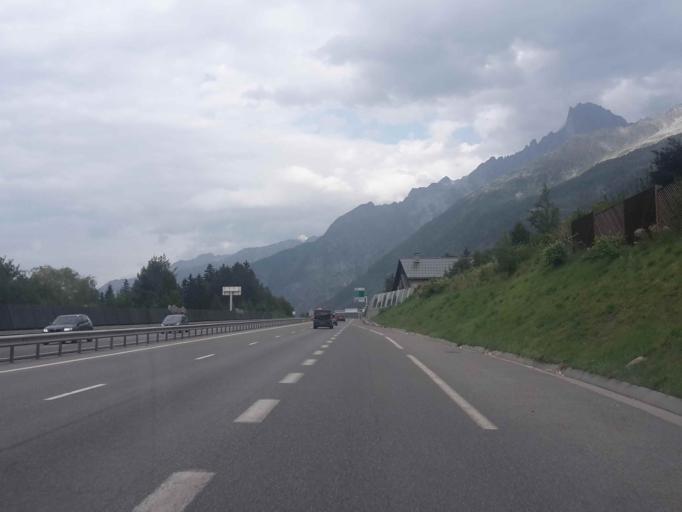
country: FR
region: Rhone-Alpes
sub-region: Departement de la Haute-Savoie
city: Chamonix-Mont-Blanc
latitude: 45.9057
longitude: 6.8427
